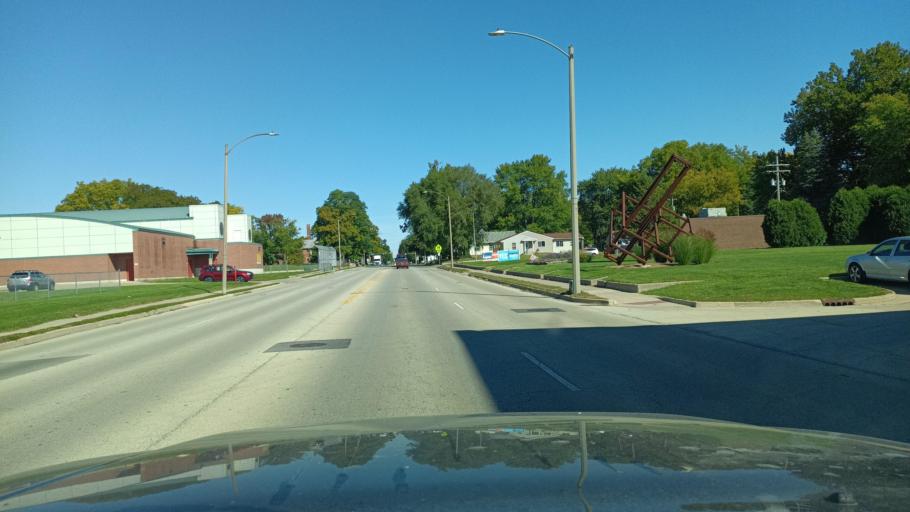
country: US
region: Illinois
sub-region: Champaign County
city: Champaign
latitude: 40.1238
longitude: -88.2435
